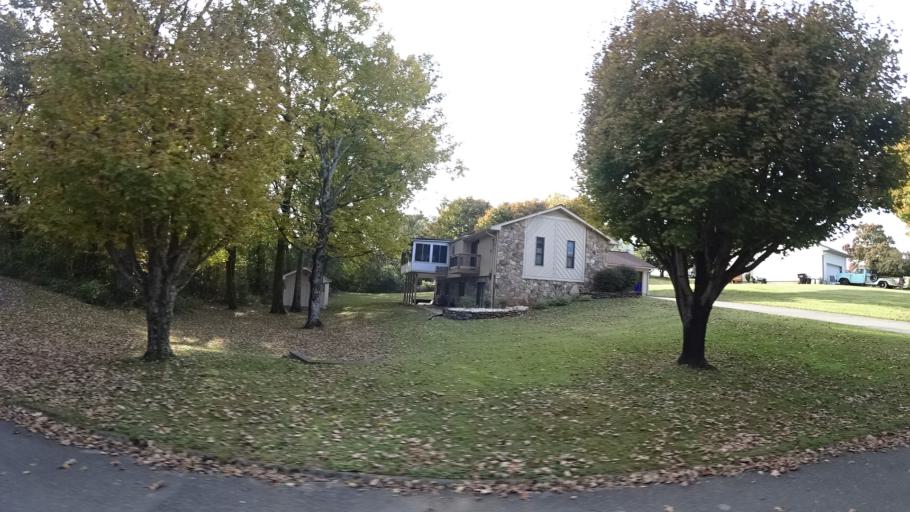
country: US
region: Tennessee
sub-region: Knox County
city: Farragut
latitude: 35.9048
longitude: -84.1612
